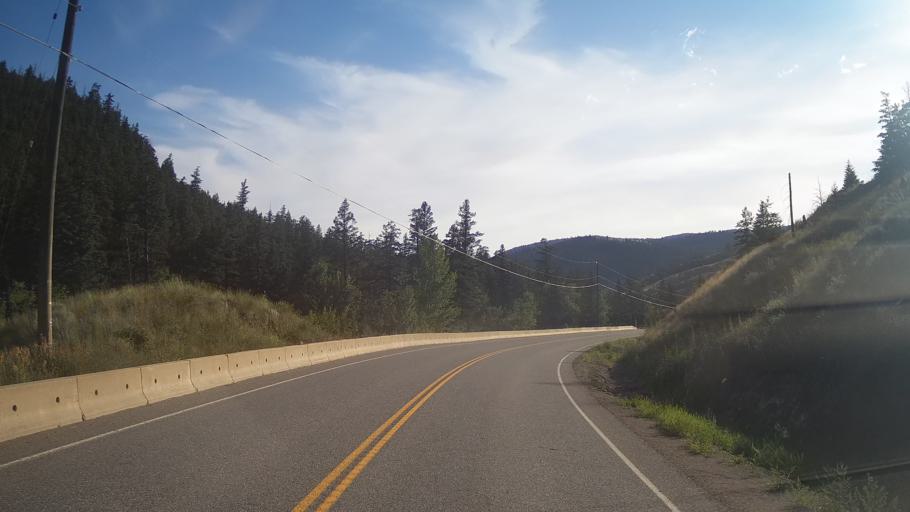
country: CA
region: British Columbia
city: Cache Creek
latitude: 50.8836
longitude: -121.4978
